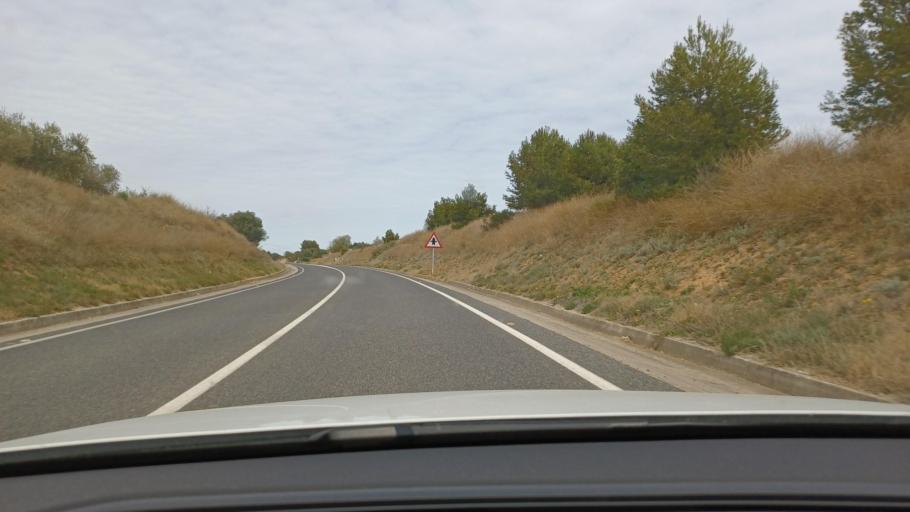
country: ES
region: Catalonia
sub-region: Provincia de Tarragona
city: Masdenverge
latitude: 40.6747
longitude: 0.5254
